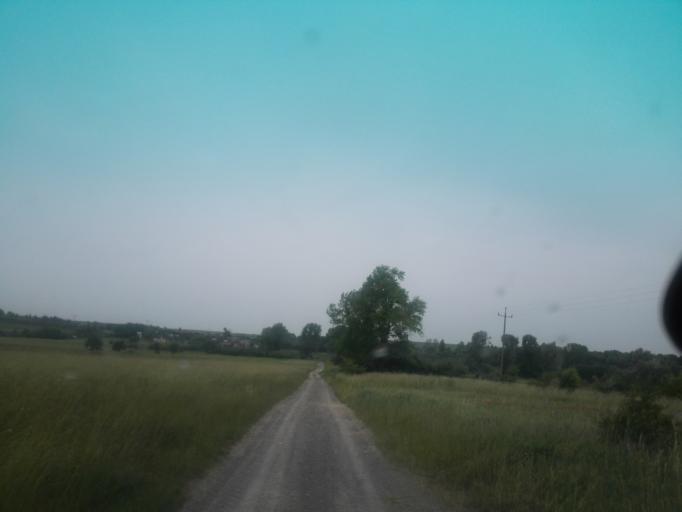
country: PL
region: Silesian Voivodeship
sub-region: Powiat czestochowski
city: Mstow
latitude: 50.7877
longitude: 19.3213
